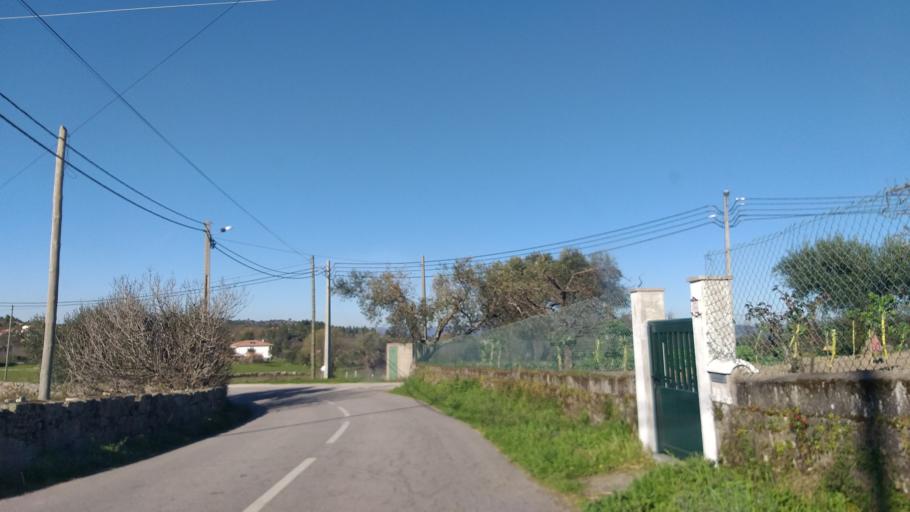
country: PT
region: Guarda
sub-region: Celorico da Beira
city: Celorico da Beira
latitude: 40.6029
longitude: -7.3609
